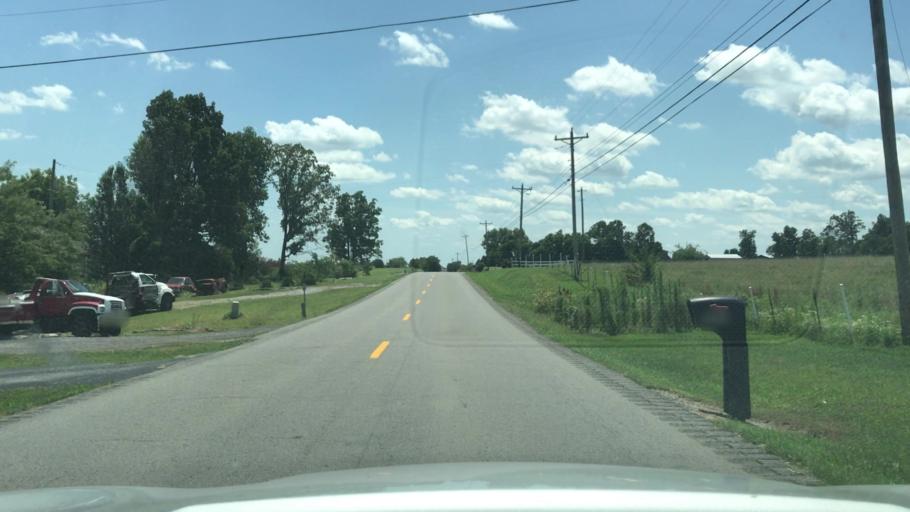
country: US
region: Kentucky
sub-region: Christian County
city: Hopkinsville
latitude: 36.9242
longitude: -87.4351
